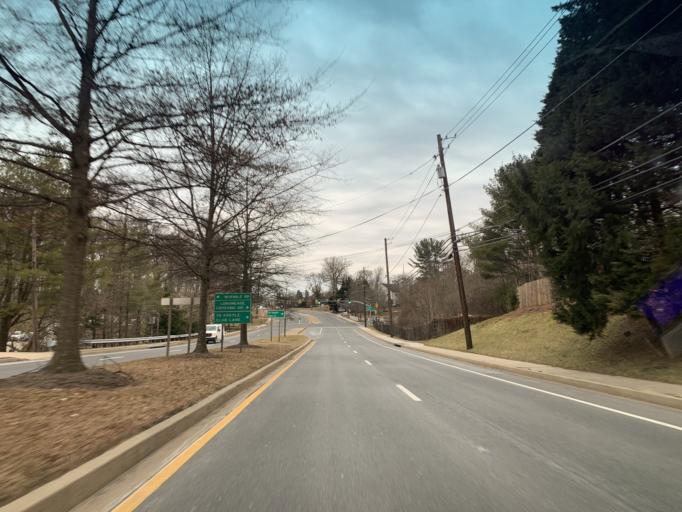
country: US
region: Maryland
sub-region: Montgomery County
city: Layhill
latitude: 39.0968
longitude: -77.0440
